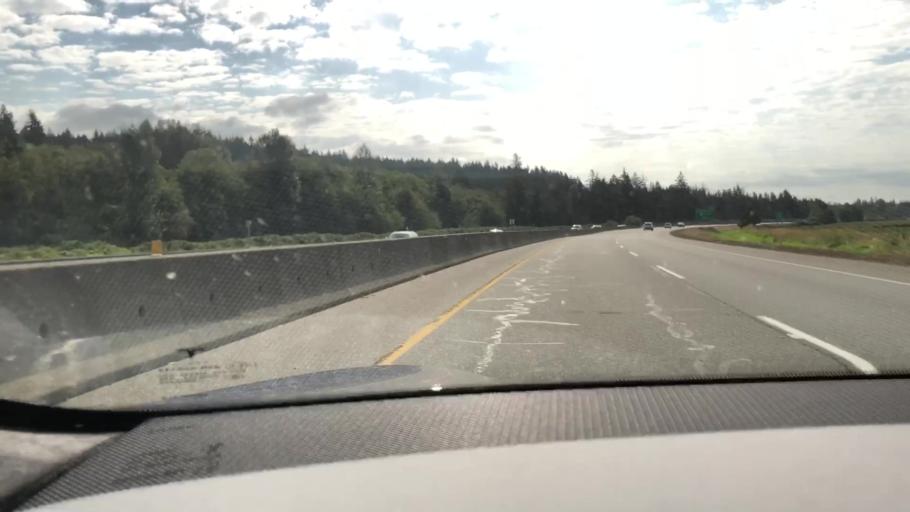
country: CA
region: British Columbia
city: Delta
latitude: 49.1121
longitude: -122.9086
